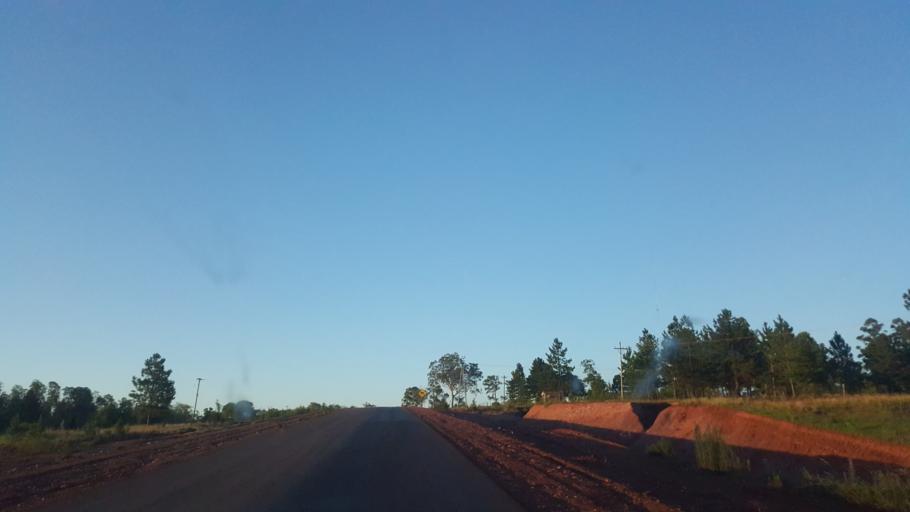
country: AR
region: Corrientes
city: Santo Tome
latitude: -28.5231
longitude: -56.0559
